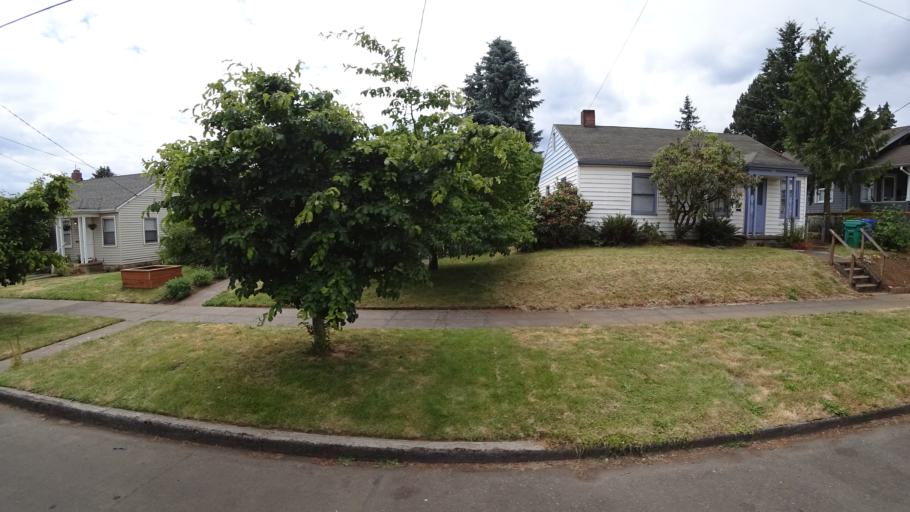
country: US
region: Oregon
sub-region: Washington County
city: West Haven
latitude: 45.5804
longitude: -122.7358
